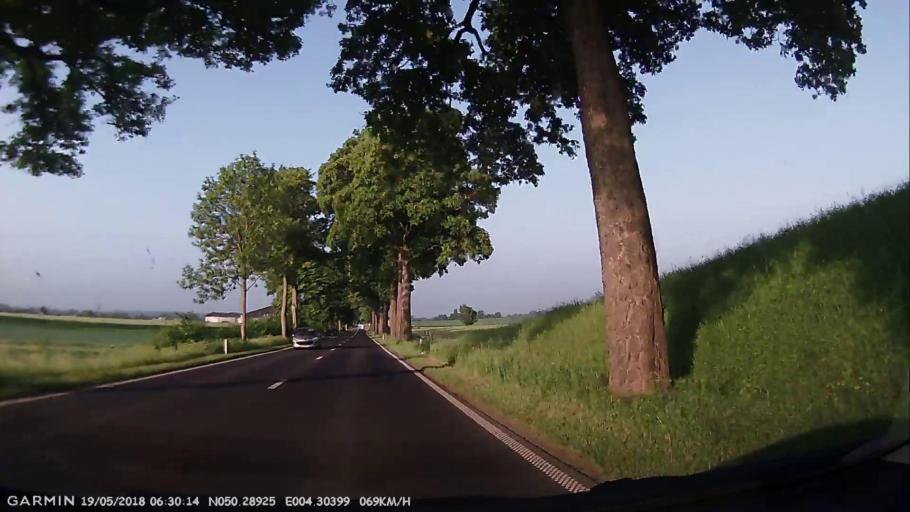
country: BE
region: Wallonia
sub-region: Province du Hainaut
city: Thuin
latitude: 50.2891
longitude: 4.3039
